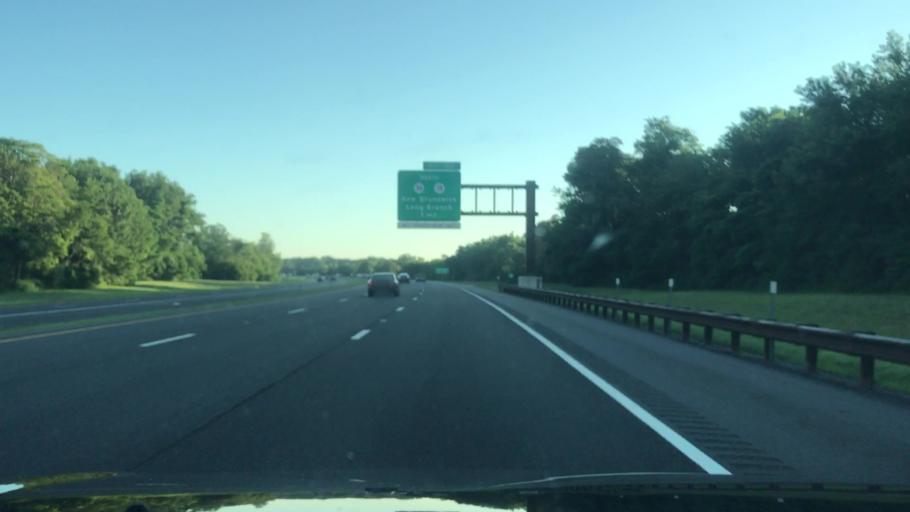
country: US
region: New Jersey
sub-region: Monmouth County
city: Eatontown
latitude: 40.2645
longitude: -74.0781
